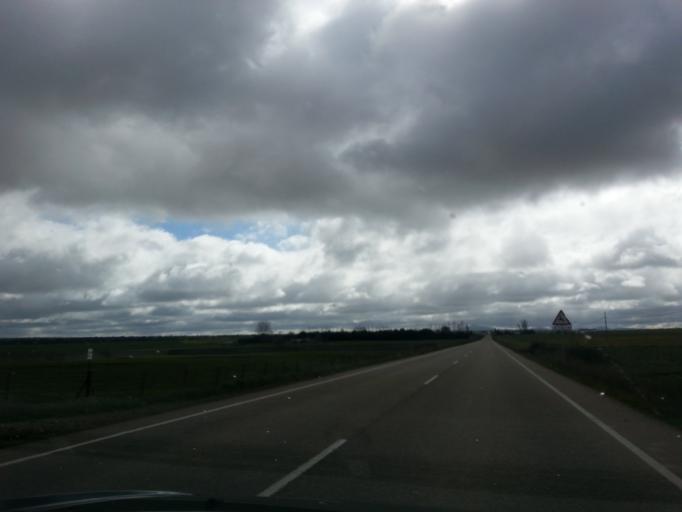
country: ES
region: Castille and Leon
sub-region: Provincia de Salamanca
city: La Fuente de San Esteban
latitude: 40.7839
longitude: -6.2364
